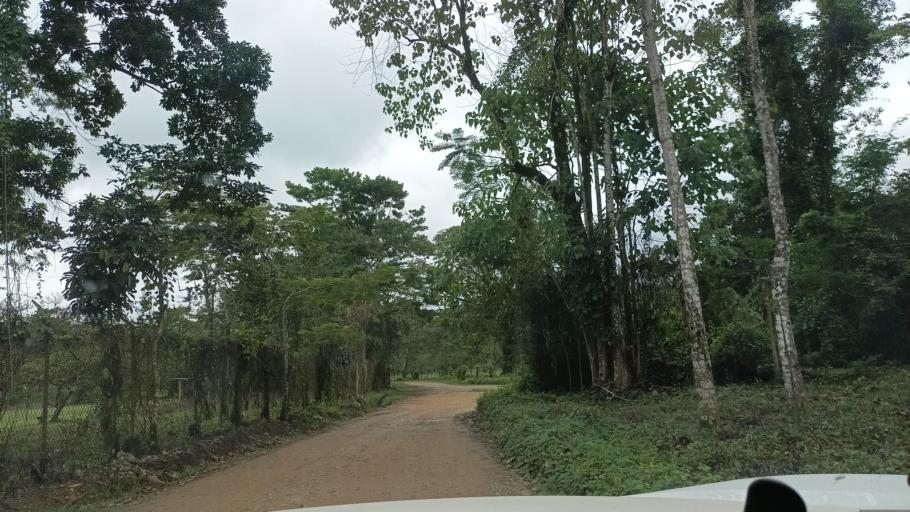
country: MX
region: Veracruz
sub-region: Uxpanapa
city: Poblado 10
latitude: 17.2713
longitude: -94.4954
